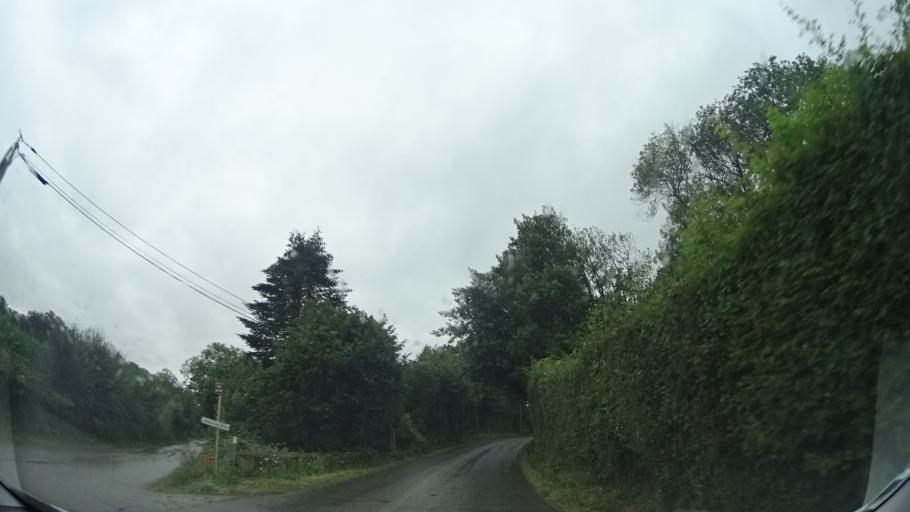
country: FR
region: Lower Normandy
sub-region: Departement de la Manche
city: Beaumont-Hague
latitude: 49.6151
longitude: -1.7986
